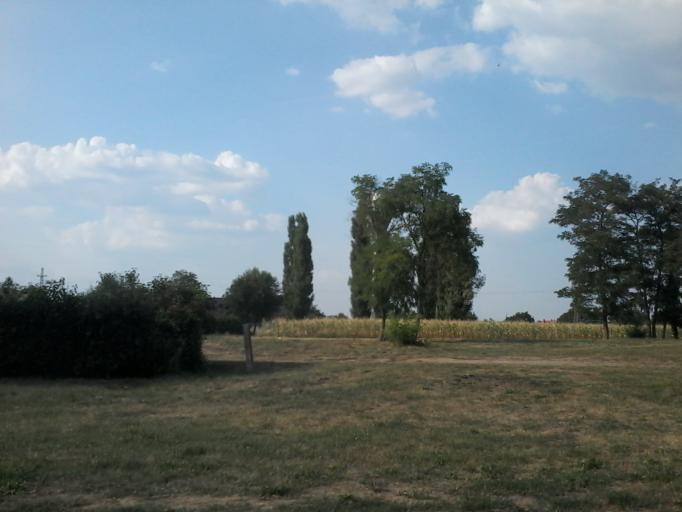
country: HU
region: Vas
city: Celldomolk
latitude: 47.2246
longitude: 17.0856
